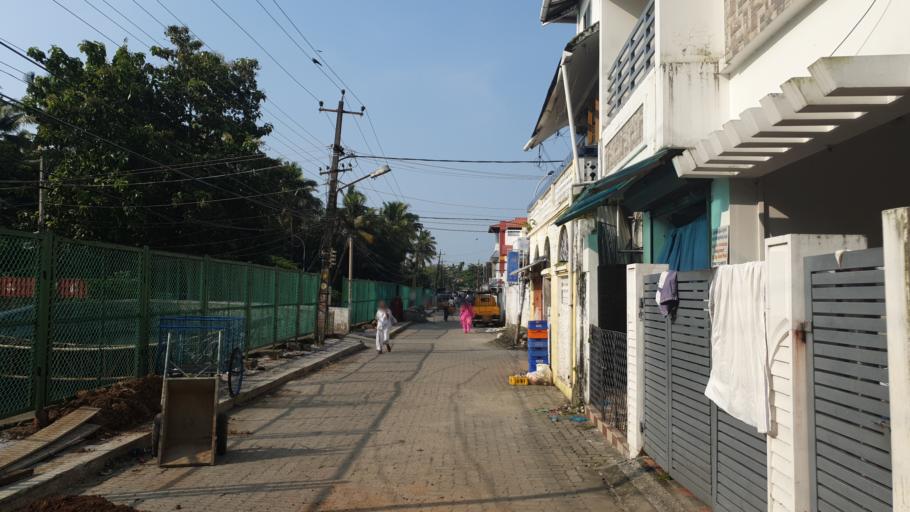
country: IN
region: Kerala
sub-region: Ernakulam
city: Cochin
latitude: 9.9612
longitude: 76.2498
